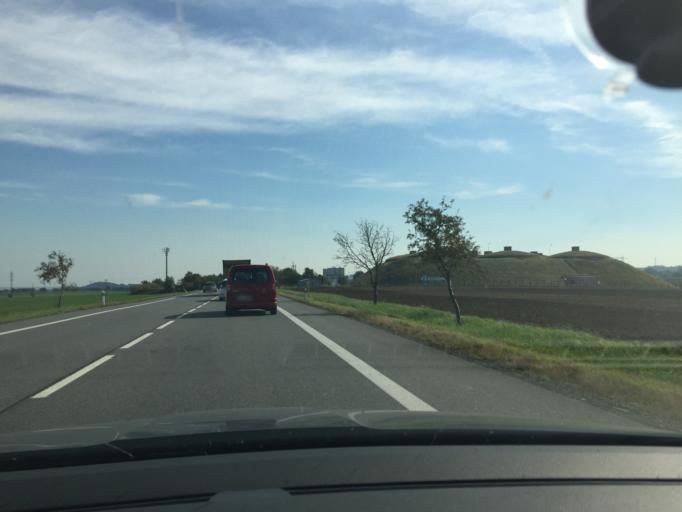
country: CZ
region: Central Bohemia
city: Cerhenice
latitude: 50.0459
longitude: 15.0681
